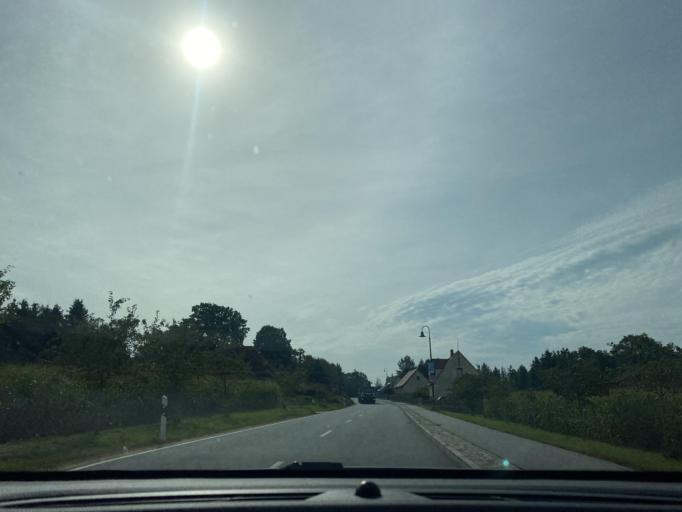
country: DE
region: Saxony
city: Reichenbach
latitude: 51.1925
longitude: 14.7586
